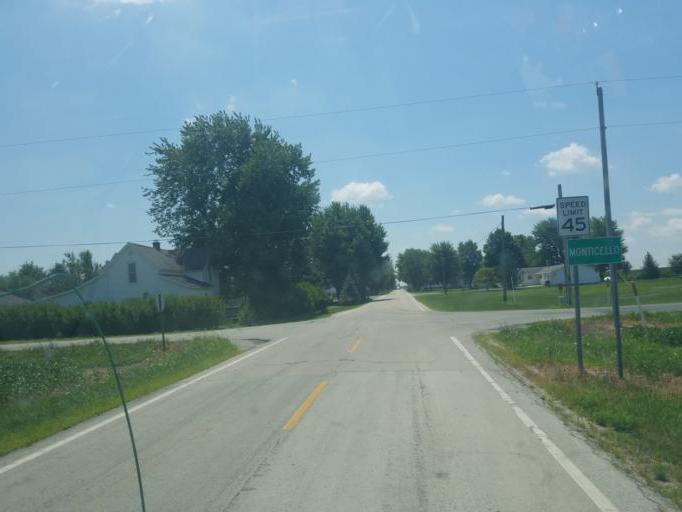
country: US
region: Ohio
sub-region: Allen County
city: Spencerville
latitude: 40.6997
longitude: -84.4256
